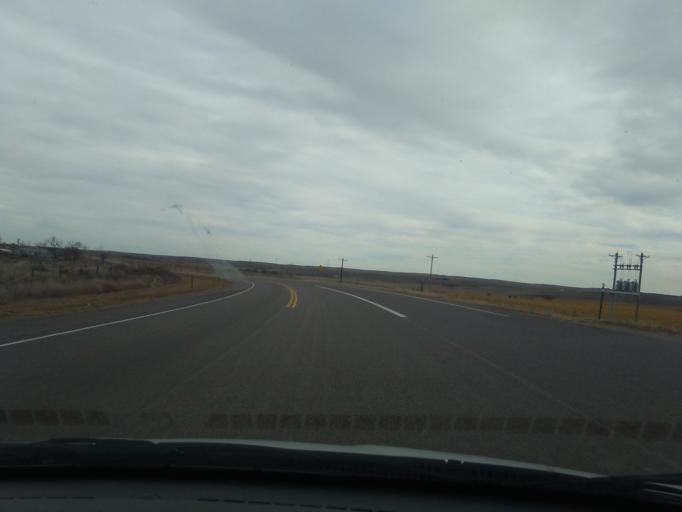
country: US
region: Colorado
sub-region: Yuma County
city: Wray
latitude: 40.0752
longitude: -102.3120
